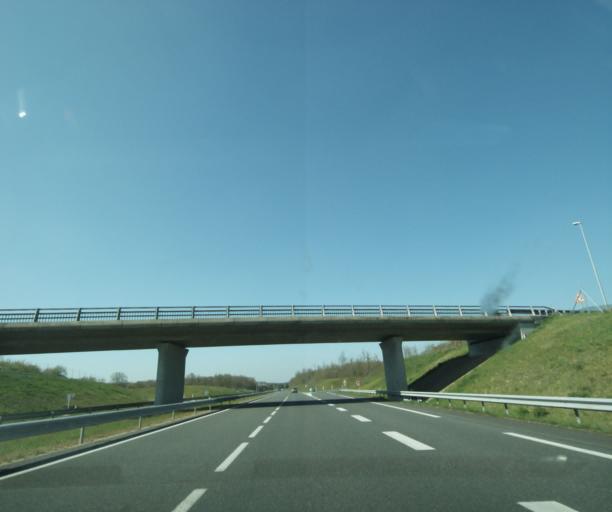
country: FR
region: Centre
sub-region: Departement du Loiret
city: Nogent-sur-Vernisson
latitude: 47.7669
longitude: 2.7158
